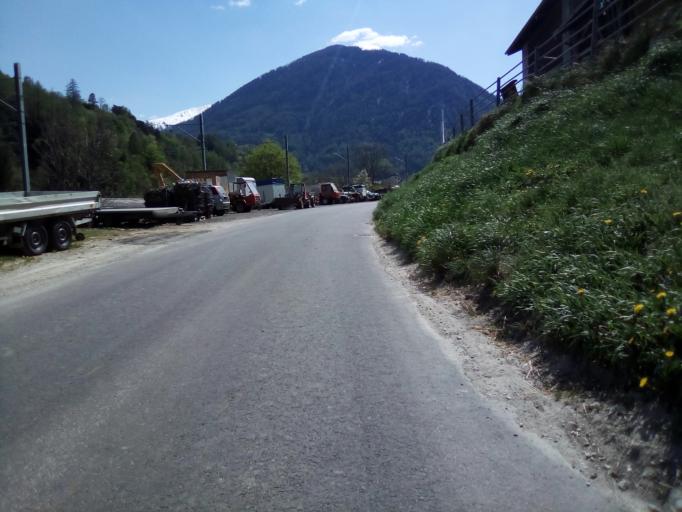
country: CH
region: Valais
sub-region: Entremont District
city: Orsieres
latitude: 46.0381
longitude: 7.1460
